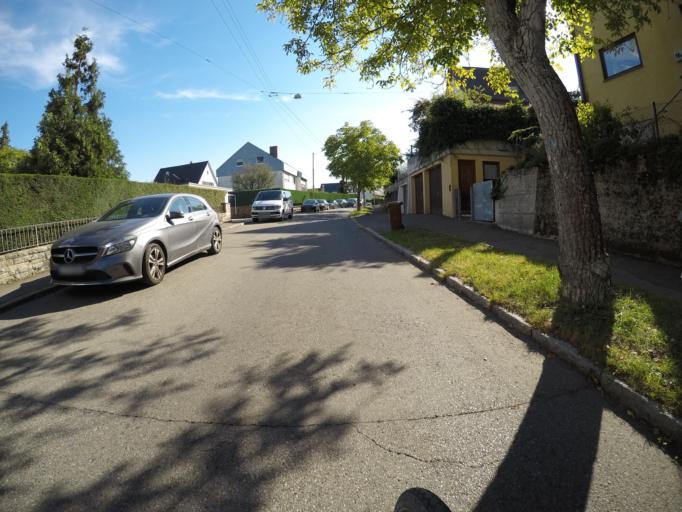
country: DE
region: Baden-Wuerttemberg
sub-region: Regierungsbezirk Stuttgart
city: Steinenbronn
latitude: 48.7202
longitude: 9.1024
